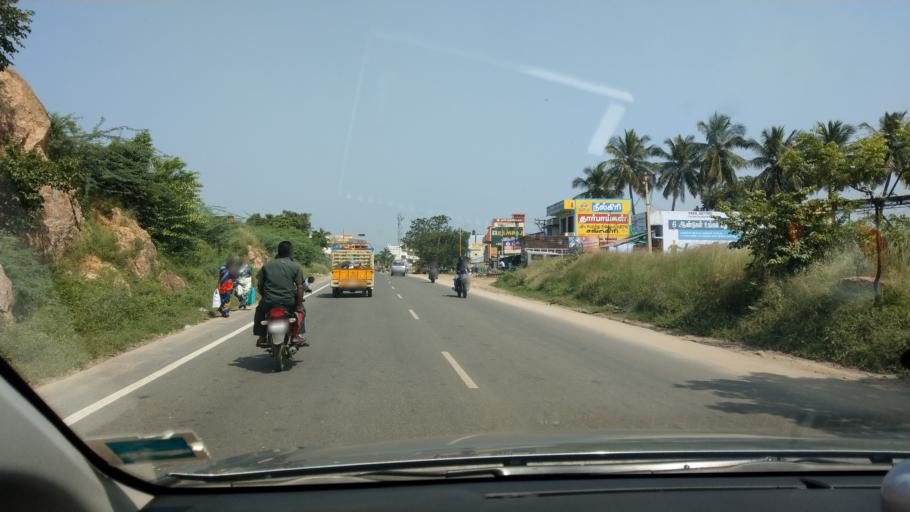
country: IN
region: Tamil Nadu
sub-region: Namakkal
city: Tiruchengode
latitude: 11.4787
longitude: 77.8788
